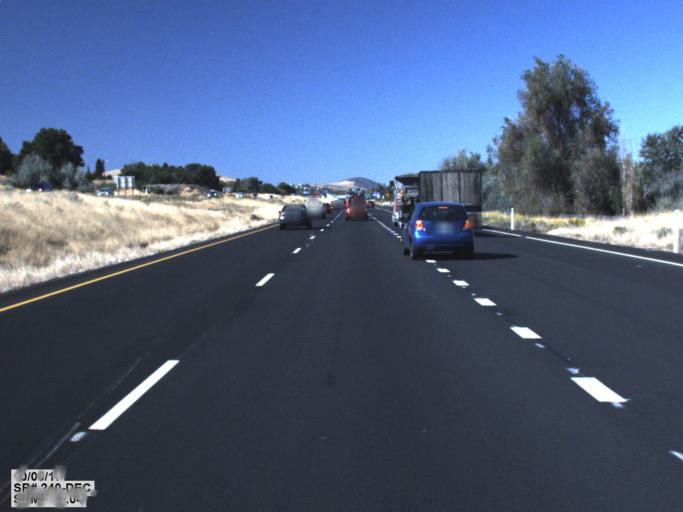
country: US
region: Washington
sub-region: Franklin County
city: West Pasco
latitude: 46.2303
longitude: -119.1999
